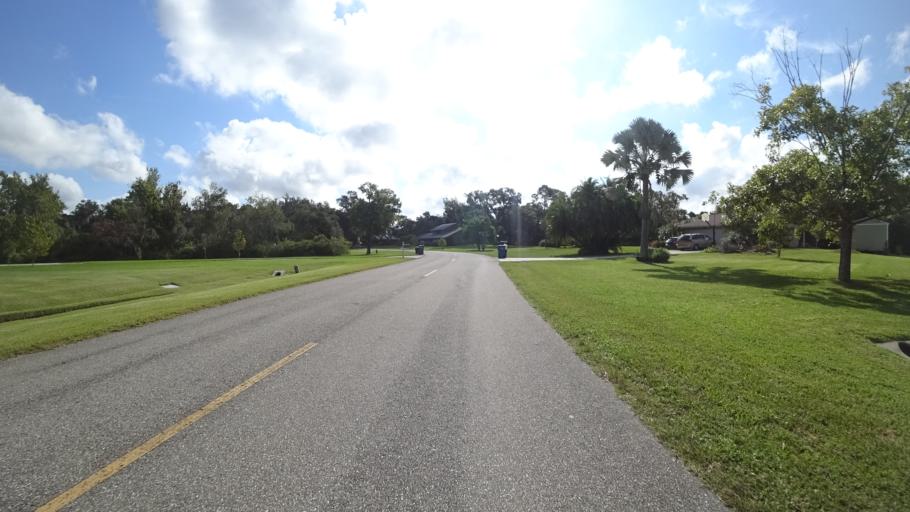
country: US
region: Florida
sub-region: Sarasota County
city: North Sarasota
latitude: 27.3988
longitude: -82.5160
